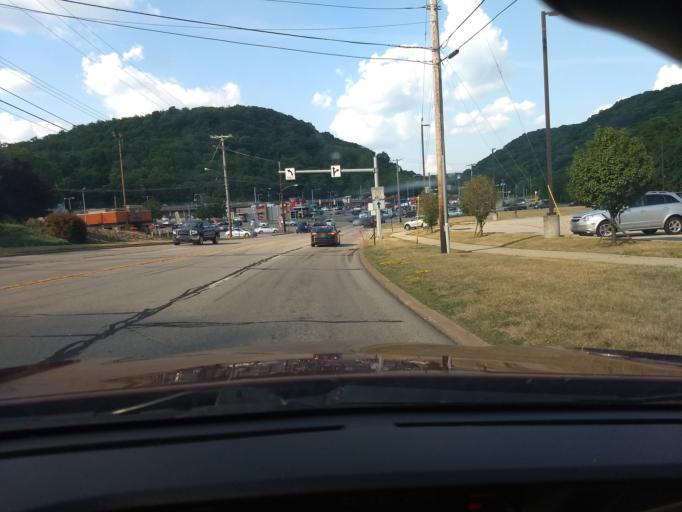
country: US
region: Pennsylvania
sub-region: Allegheny County
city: White Oak
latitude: 40.3367
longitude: -79.8099
